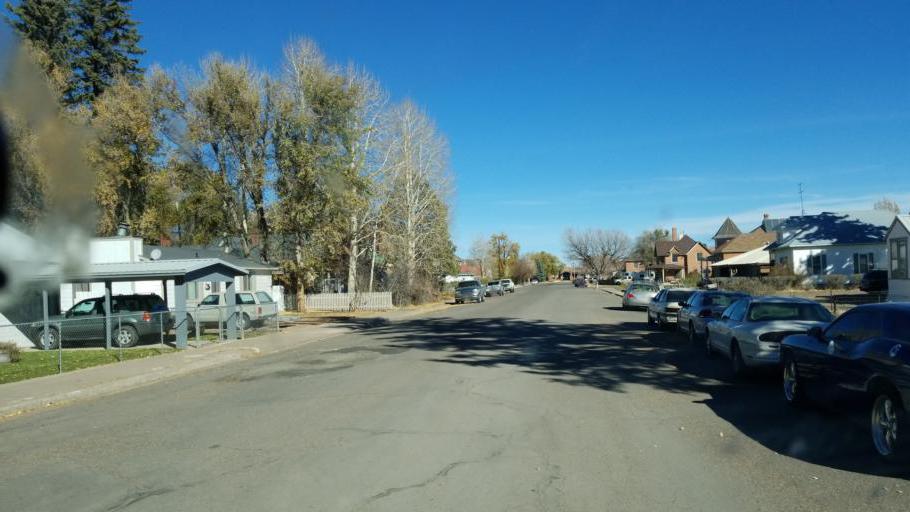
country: US
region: Colorado
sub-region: Rio Grande County
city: Monte Vista
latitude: 37.5768
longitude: -106.1509
